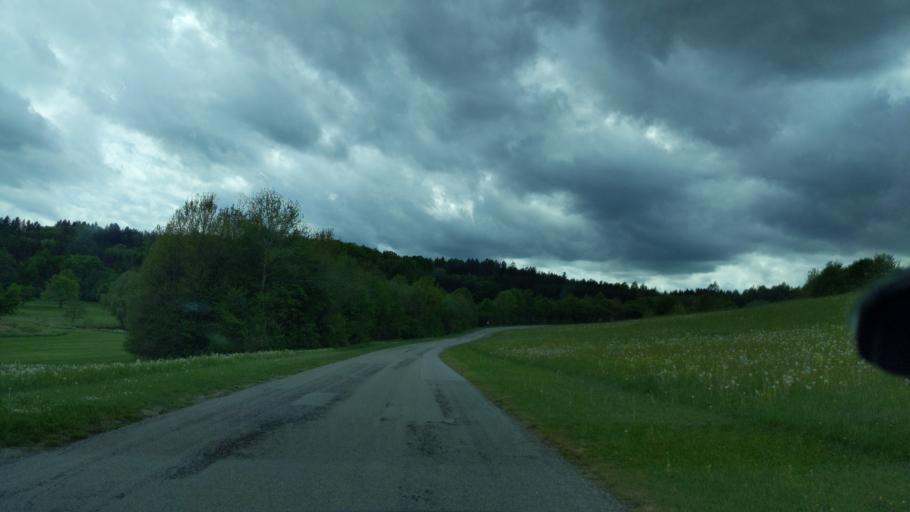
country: DE
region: Bavaria
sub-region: Upper Bavaria
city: Steinhoring
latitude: 48.1102
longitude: 11.9988
